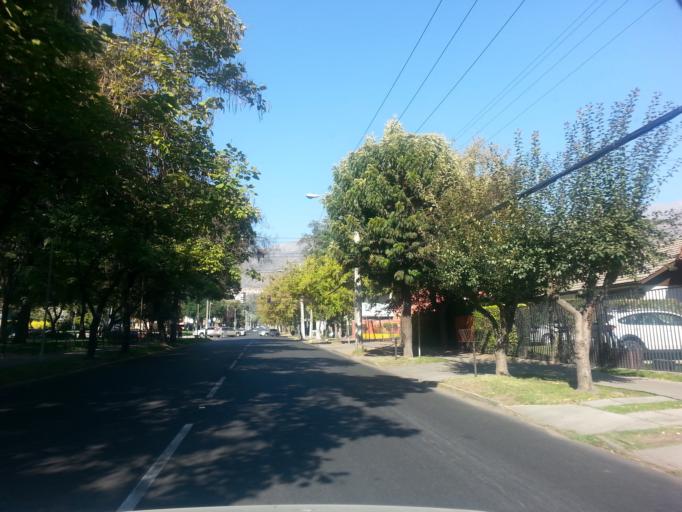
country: CL
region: Santiago Metropolitan
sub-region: Provincia de Santiago
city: Villa Presidente Frei, Nunoa, Santiago, Chile
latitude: -33.4248
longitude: -70.5474
